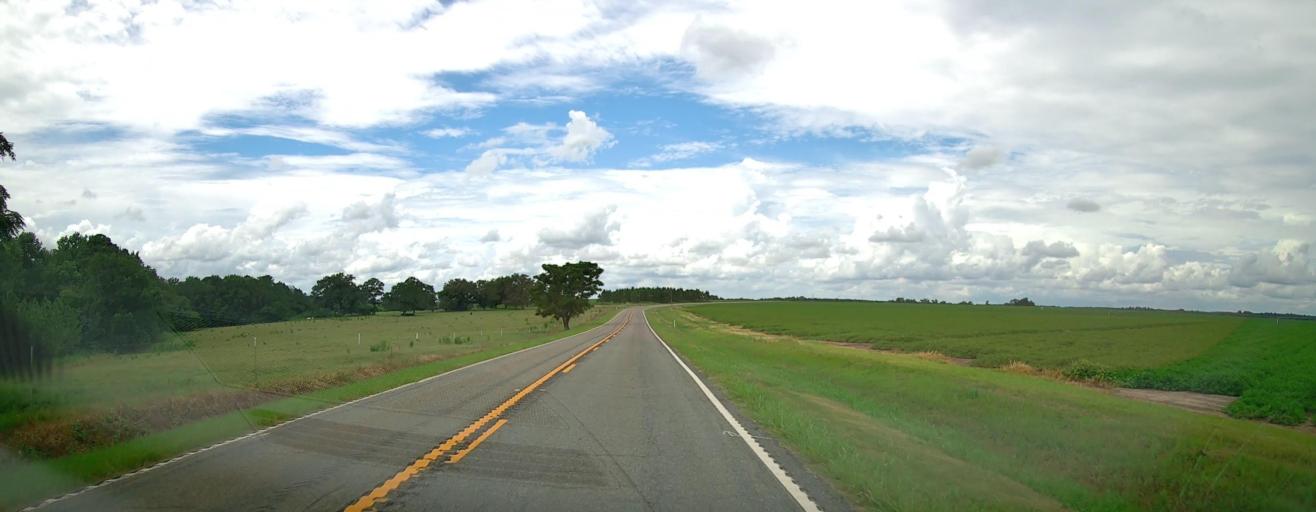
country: US
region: Georgia
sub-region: Dooly County
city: Unadilla
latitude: 32.2615
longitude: -83.8068
